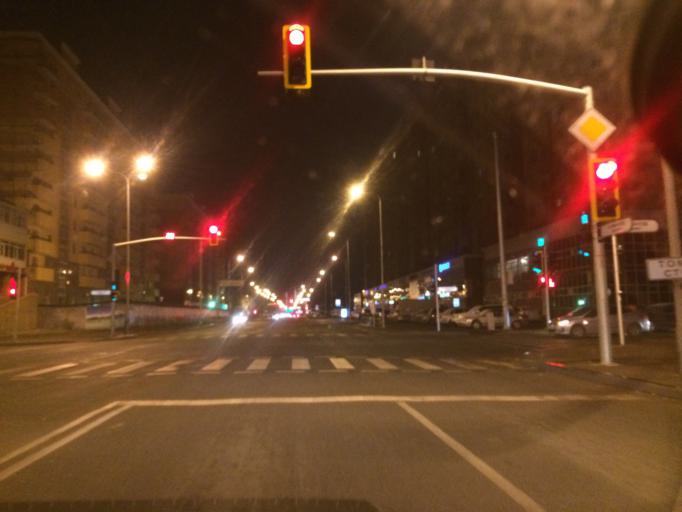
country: KZ
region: Astana Qalasy
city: Astana
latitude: 51.1608
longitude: 71.4595
